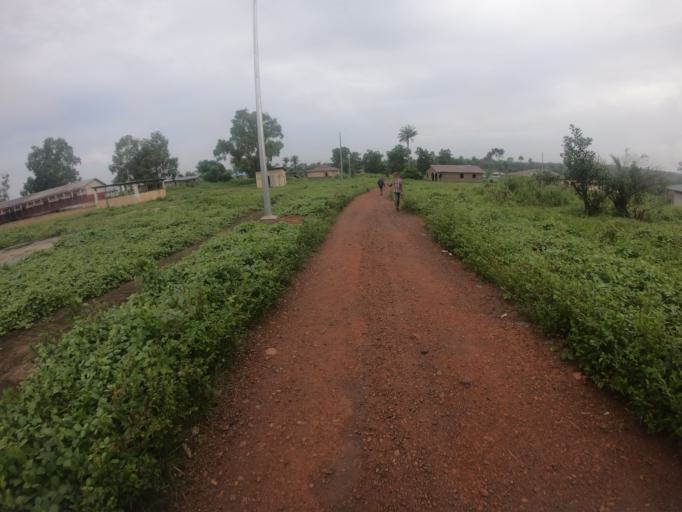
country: SL
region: Northern Province
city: Port Loko
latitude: 8.4948
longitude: -12.7506
